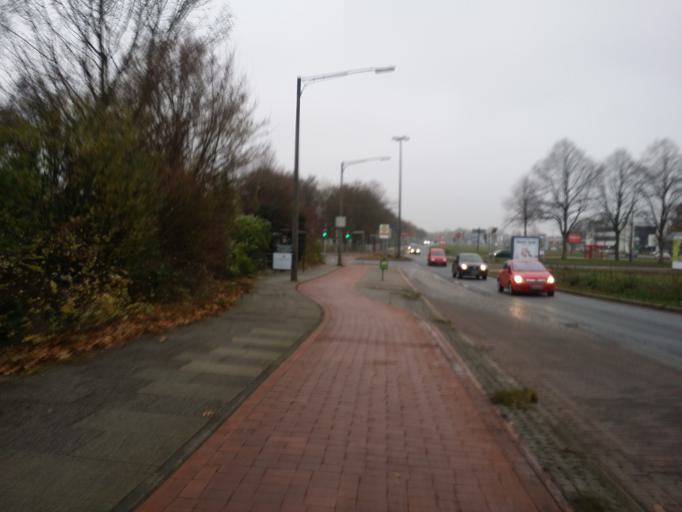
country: DE
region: Bremen
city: Bremen
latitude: 53.0511
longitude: 8.8491
